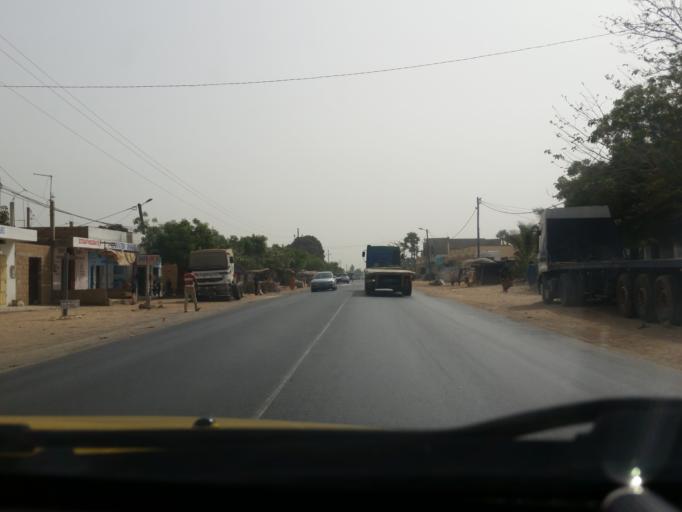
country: SN
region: Thies
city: Pout
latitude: 14.7469
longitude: -17.1327
